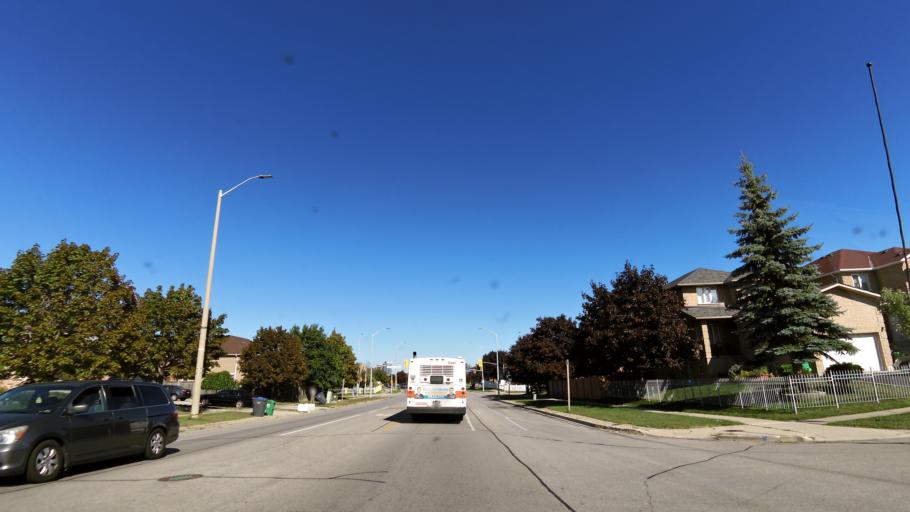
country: CA
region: Ontario
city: Mississauga
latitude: 43.5999
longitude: -79.6774
